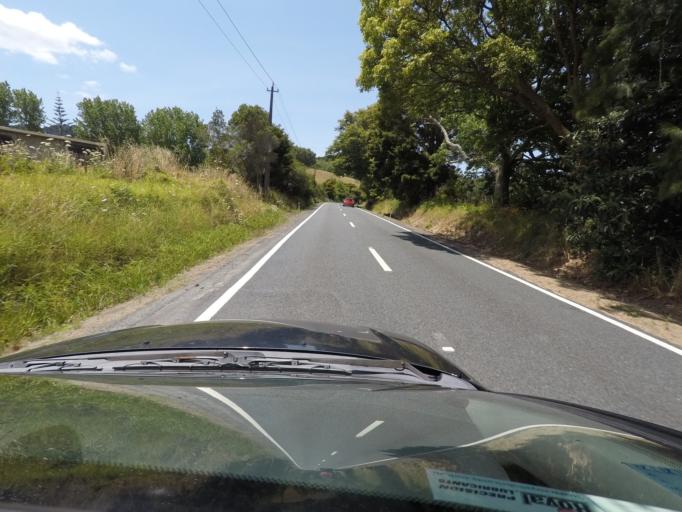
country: NZ
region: Auckland
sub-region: Auckland
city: Warkworth
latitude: -36.3196
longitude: 174.7338
